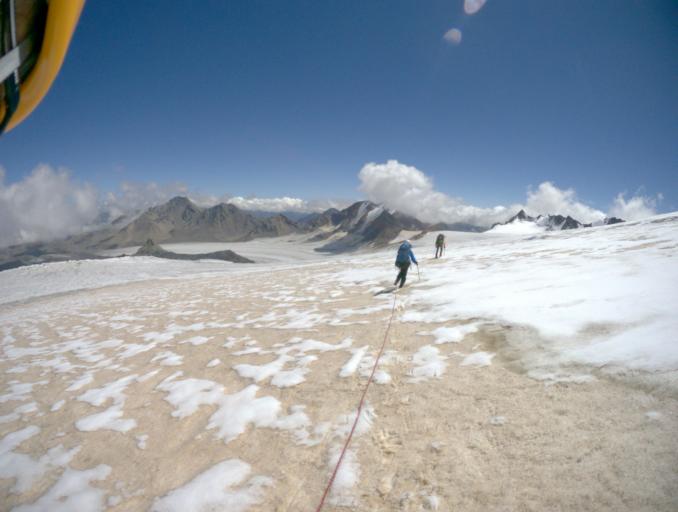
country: RU
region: Kabardino-Balkariya
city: Terskol
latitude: 43.3536
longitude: 42.5038
